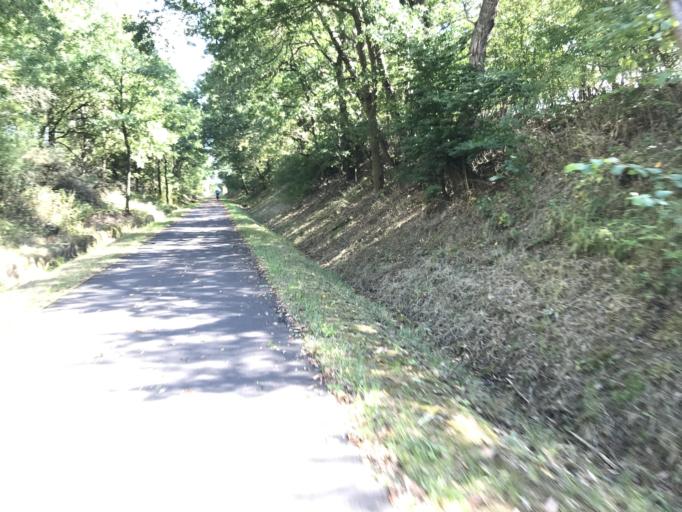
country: DE
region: Hesse
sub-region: Regierungsbezirk Kassel
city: Sachsenhausen
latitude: 51.2400
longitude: 9.0387
